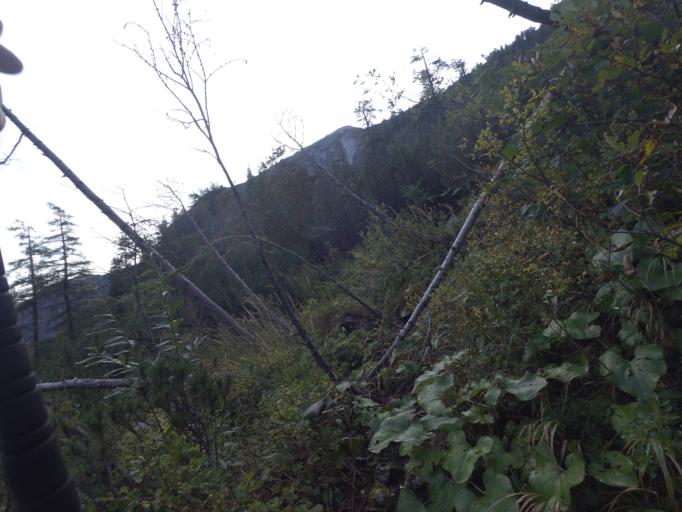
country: AT
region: Salzburg
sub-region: Politischer Bezirk Sankt Johann im Pongau
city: Untertauern
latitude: 47.2316
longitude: 13.4208
